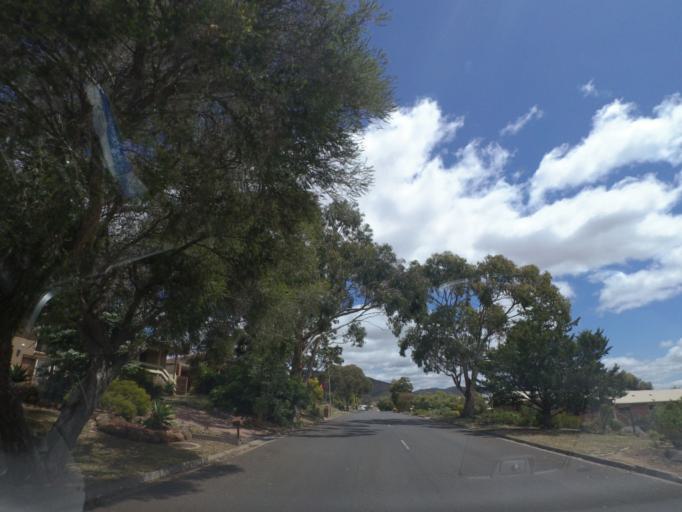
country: AU
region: Victoria
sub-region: Moorabool
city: Bacchus Marsh
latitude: -37.6391
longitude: 144.4259
